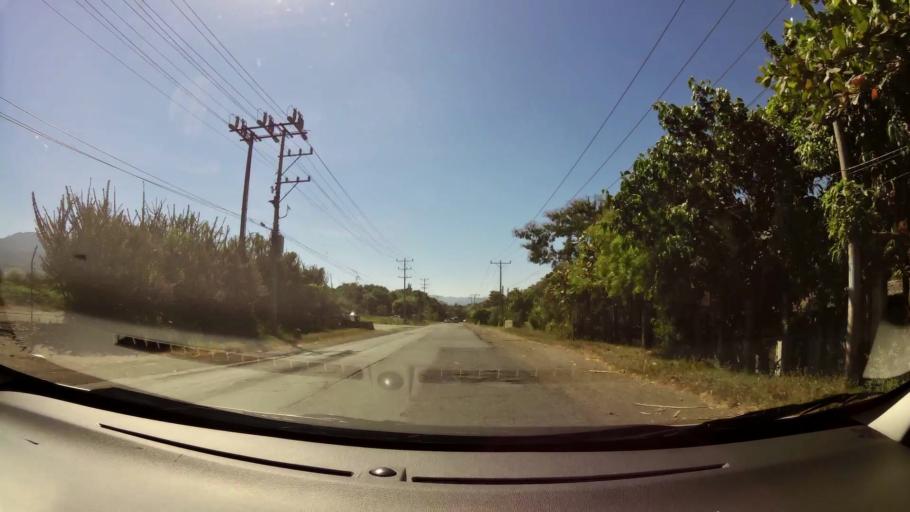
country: SV
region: La Libertad
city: San Juan Opico
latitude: 13.8056
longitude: -89.3588
